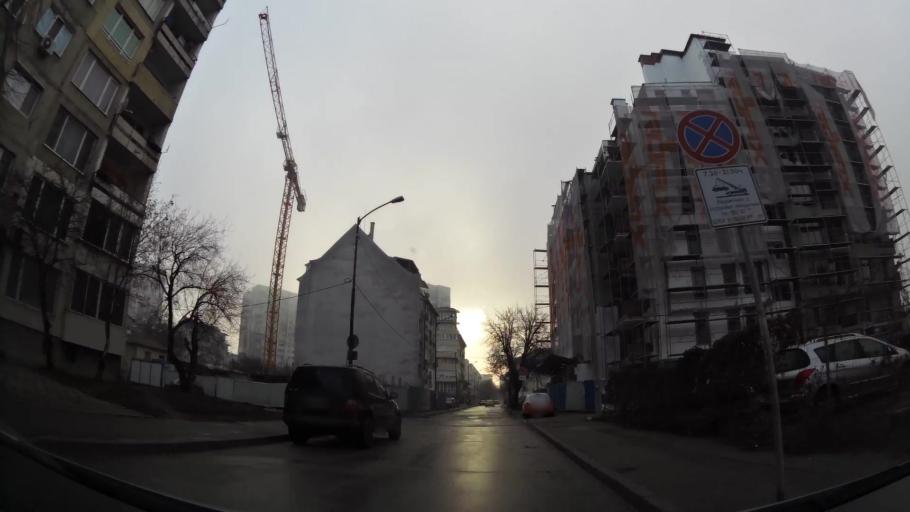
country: BG
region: Sofia-Capital
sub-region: Stolichna Obshtina
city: Sofia
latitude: 42.7313
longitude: 23.3033
